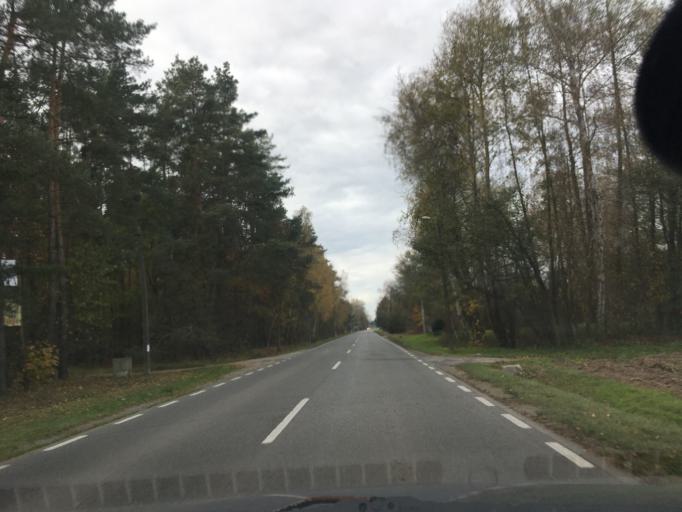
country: PL
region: Masovian Voivodeship
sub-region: Powiat piaseczynski
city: Tarczyn
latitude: 51.9788
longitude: 20.8679
